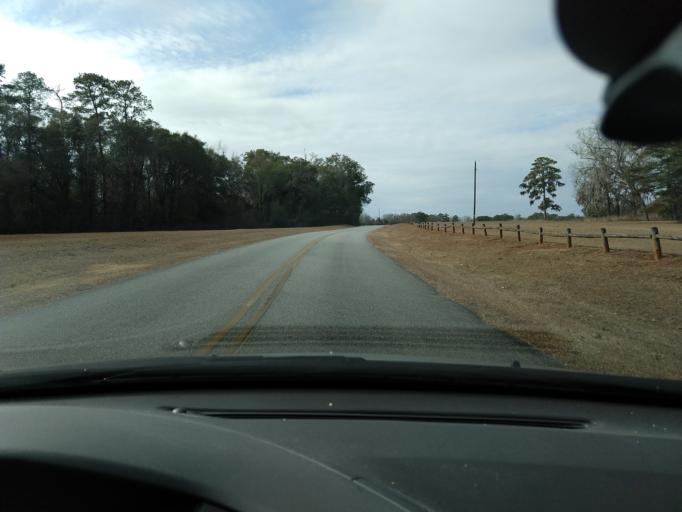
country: US
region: Georgia
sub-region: Early County
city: Blakely
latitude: 31.4686
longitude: -84.9380
